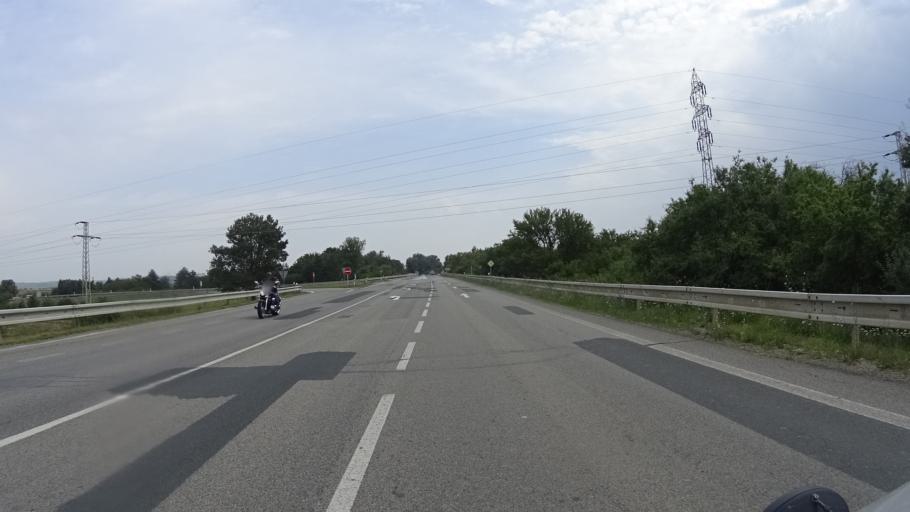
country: CZ
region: South Moravian
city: Podivin
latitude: 48.8311
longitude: 16.8664
